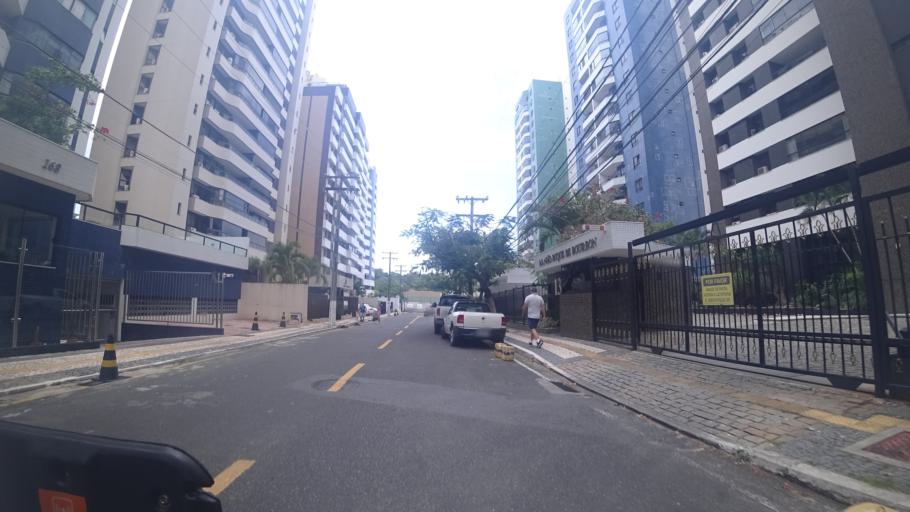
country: BR
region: Bahia
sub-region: Salvador
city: Salvador
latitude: -12.9989
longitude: -38.4675
